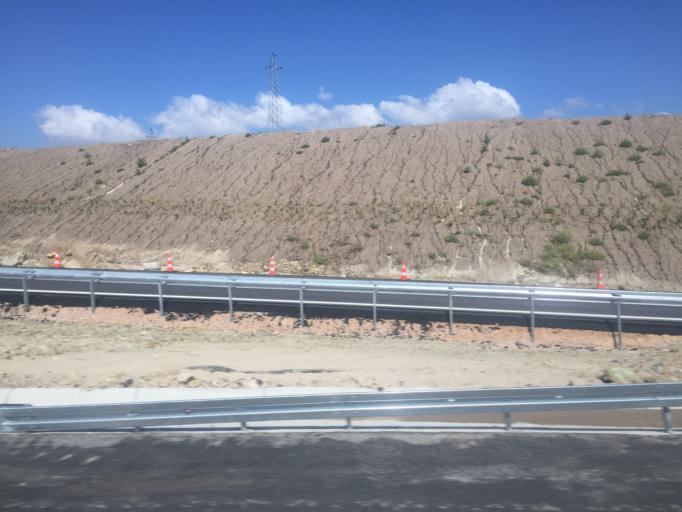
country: TR
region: Balikesir
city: Gobel
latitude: 40.0437
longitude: 28.2228
